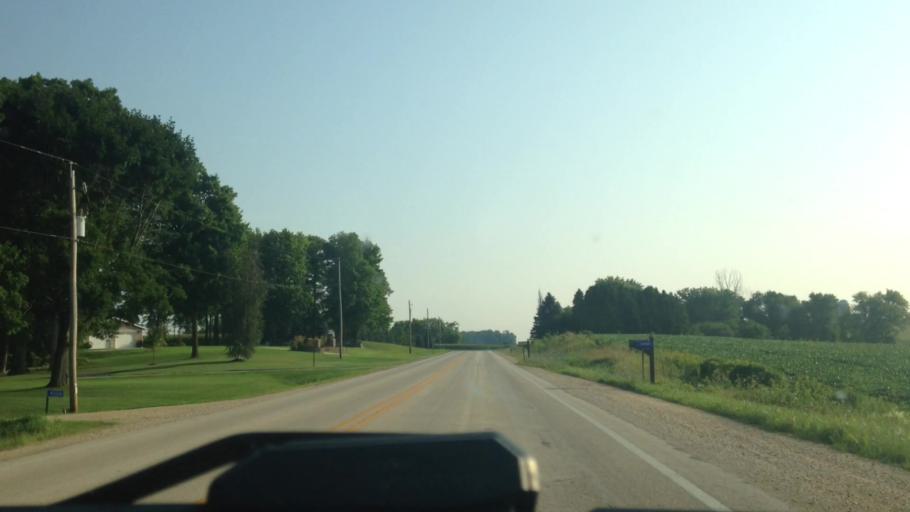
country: US
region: Wisconsin
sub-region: Dodge County
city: Theresa
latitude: 43.5331
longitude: -88.4973
